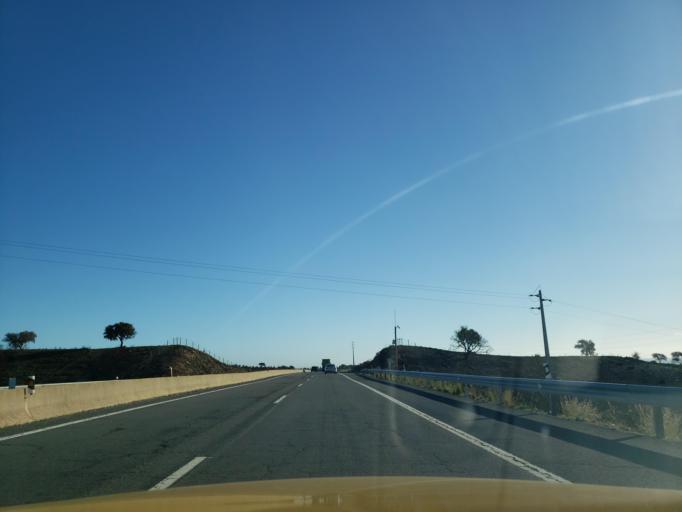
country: PT
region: Faro
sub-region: Tavira
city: Tavira
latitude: 37.1853
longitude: -7.5693
